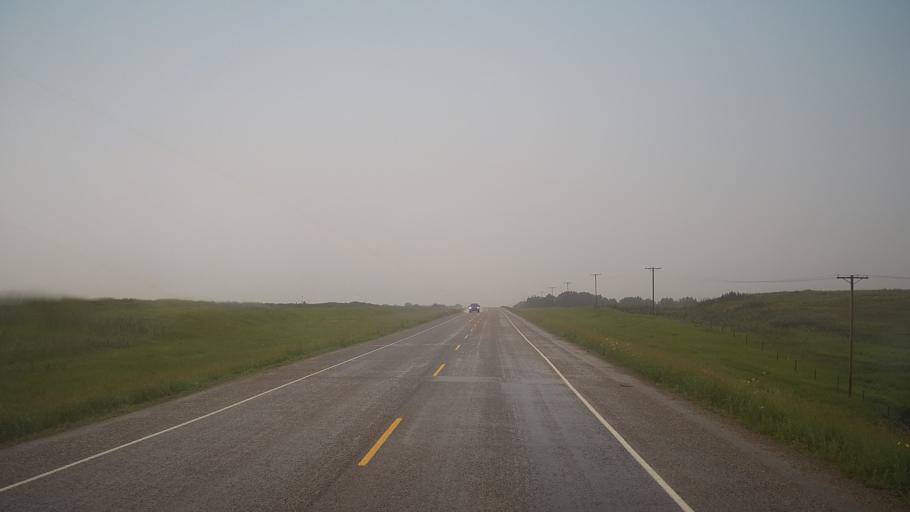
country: CA
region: Saskatchewan
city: Biggar
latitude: 52.1323
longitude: -108.1546
